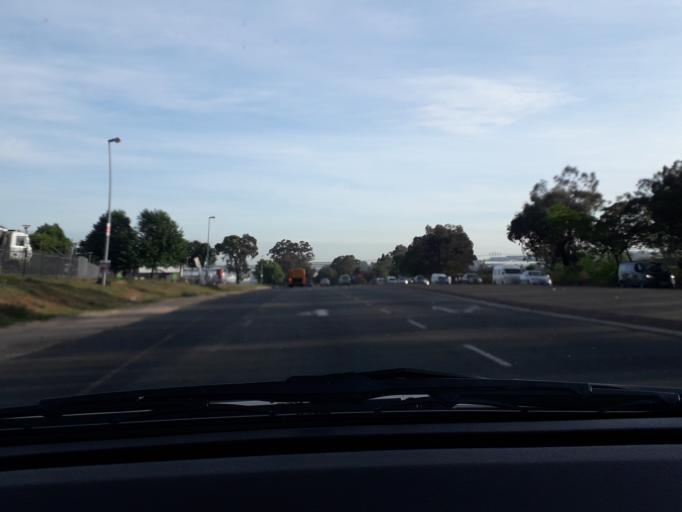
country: ZA
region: Gauteng
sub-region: City of Johannesburg Metropolitan Municipality
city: Midrand
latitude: -25.9385
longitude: 28.1457
